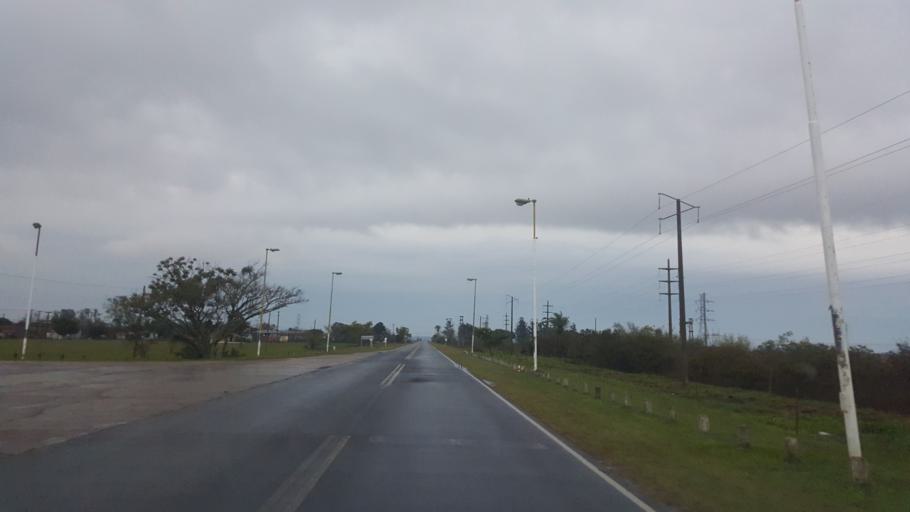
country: AR
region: Corrientes
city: Ituzaingo
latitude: -27.5692
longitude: -56.6655
